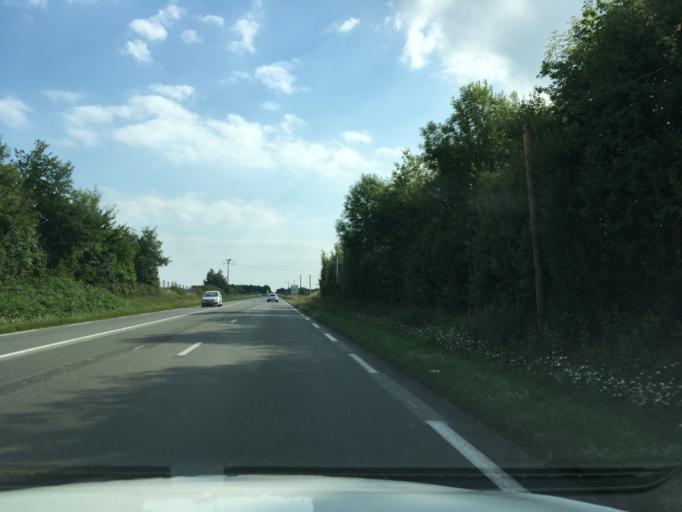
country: FR
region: Poitou-Charentes
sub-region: Departement des Deux-Sevres
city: Saint-Pardoux
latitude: 46.5531
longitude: -0.3090
